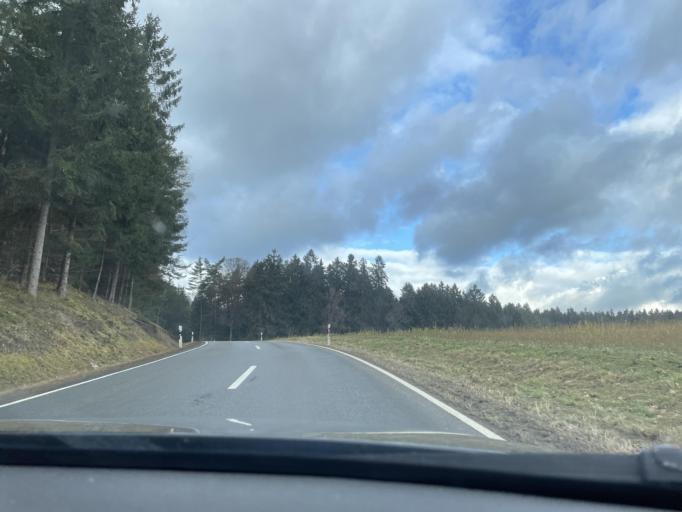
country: DE
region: Bavaria
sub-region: Upper Palatinate
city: Blaibach
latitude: 49.1812
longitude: 12.7933
